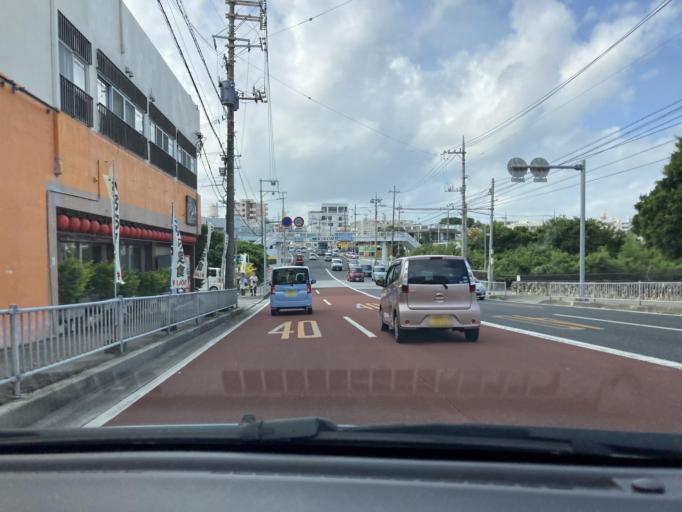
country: JP
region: Okinawa
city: Ginowan
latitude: 26.2590
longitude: 127.7420
